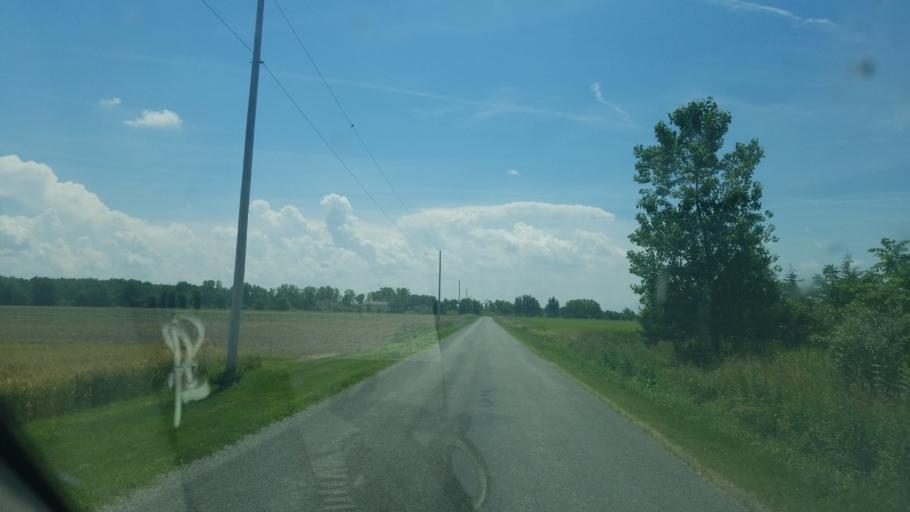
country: US
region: Ohio
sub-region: Hancock County
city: Findlay
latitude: 40.9973
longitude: -83.6362
